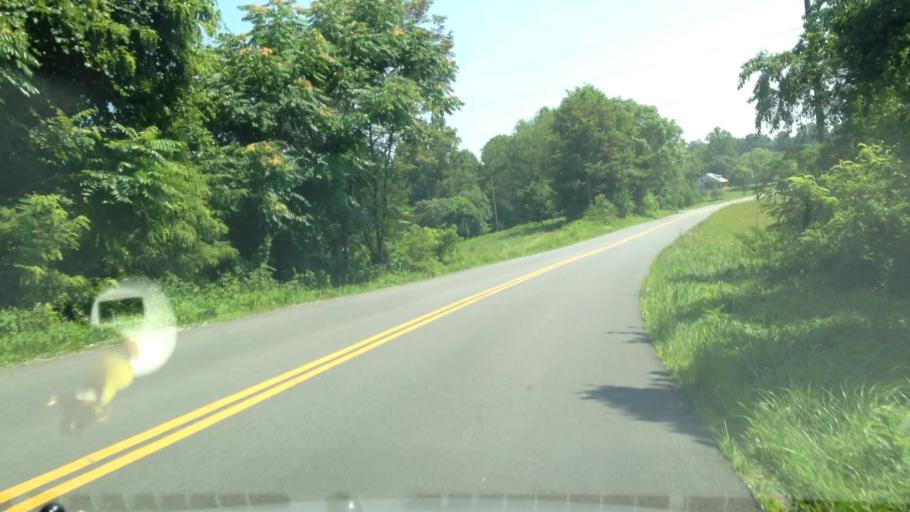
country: US
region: Virginia
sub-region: Patrick County
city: Patrick Springs
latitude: 36.5835
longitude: -80.1907
